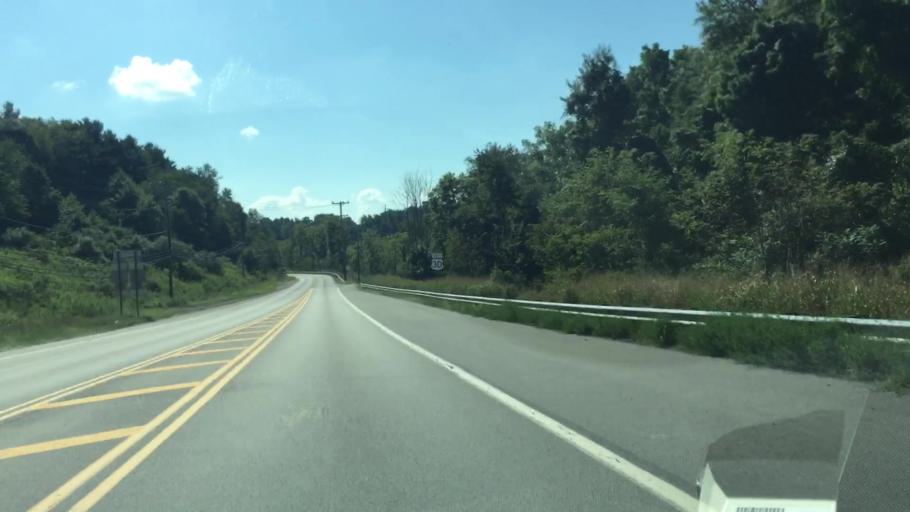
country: US
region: Pennsylvania
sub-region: Allegheny County
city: Imperial
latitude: 40.4712
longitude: -80.2801
